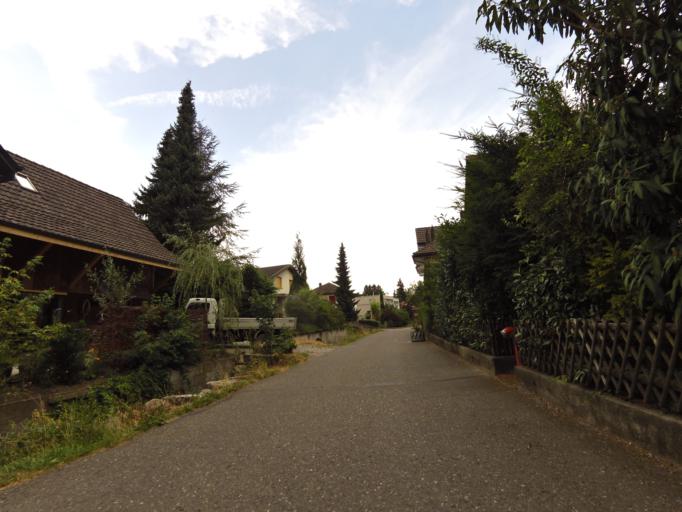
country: CH
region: Aargau
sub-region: Bezirk Aarau
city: Suhr
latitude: 47.3757
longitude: 8.0767
